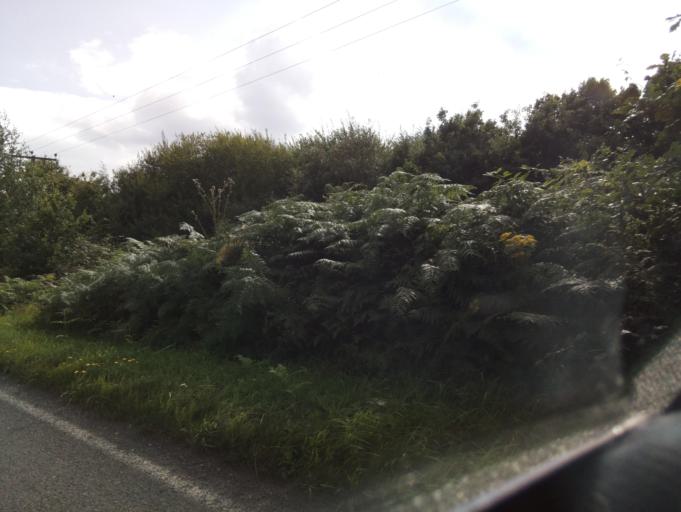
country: GB
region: England
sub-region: Hampshire
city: Marchwood
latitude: 50.8703
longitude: -1.4389
